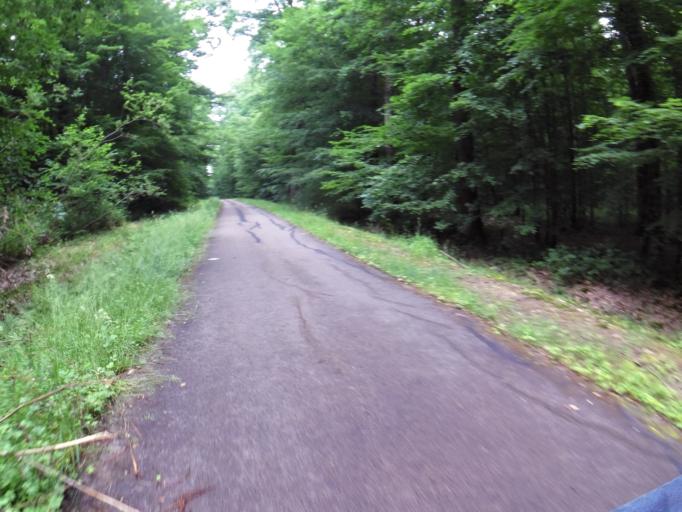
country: FR
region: Champagne-Ardenne
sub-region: Departement de la Haute-Marne
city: Montier-en-Der
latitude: 48.5444
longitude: 4.8167
